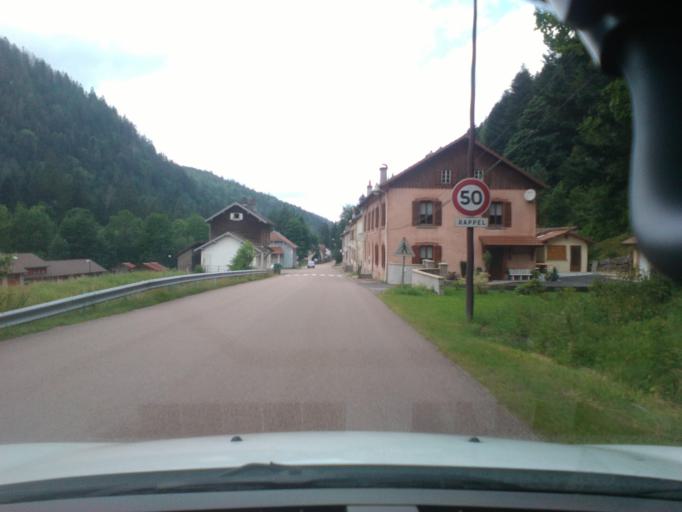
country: FR
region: Lorraine
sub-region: Departement des Vosges
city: Gerardmer
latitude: 48.1002
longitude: 6.8765
